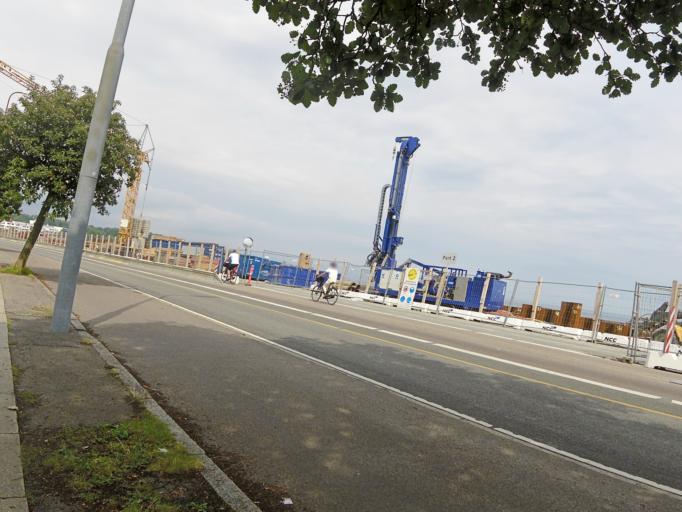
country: DK
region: Capital Region
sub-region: Gentofte Kommune
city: Charlottenlund
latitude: 55.7721
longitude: 12.5955
